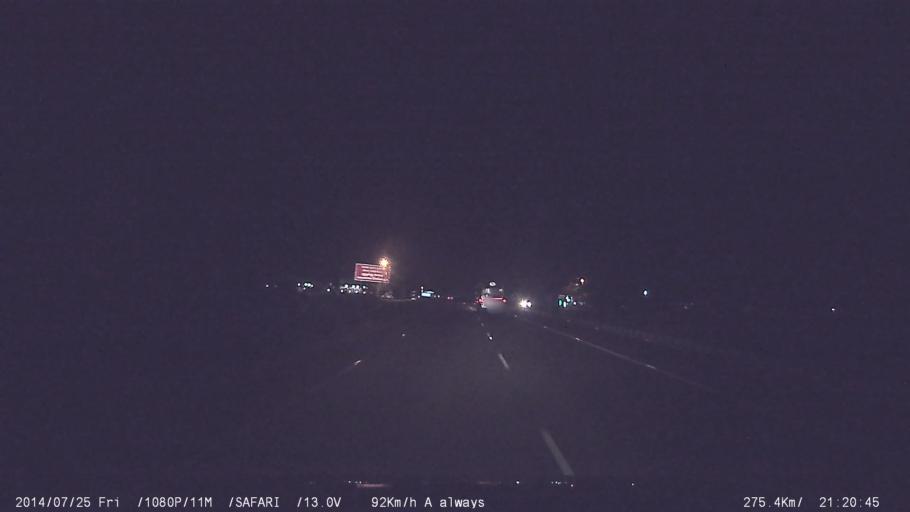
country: IN
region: Tamil Nadu
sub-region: Erode
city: Perundurai
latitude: 11.2915
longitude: 77.5791
